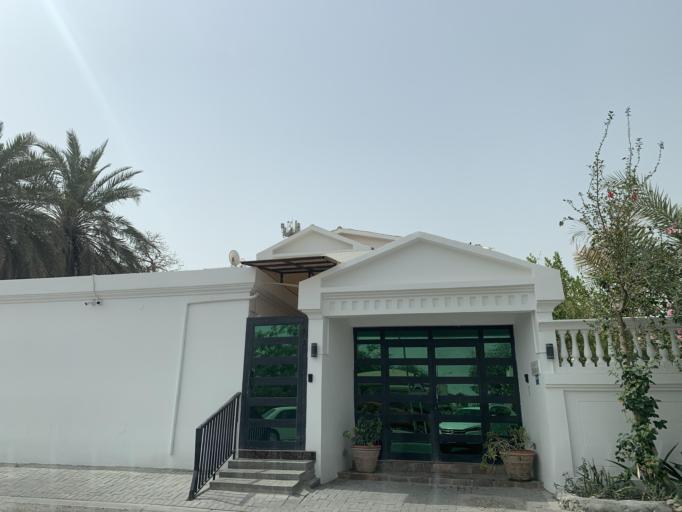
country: BH
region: Northern
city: Madinat `Isa
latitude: 26.1666
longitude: 50.5547
